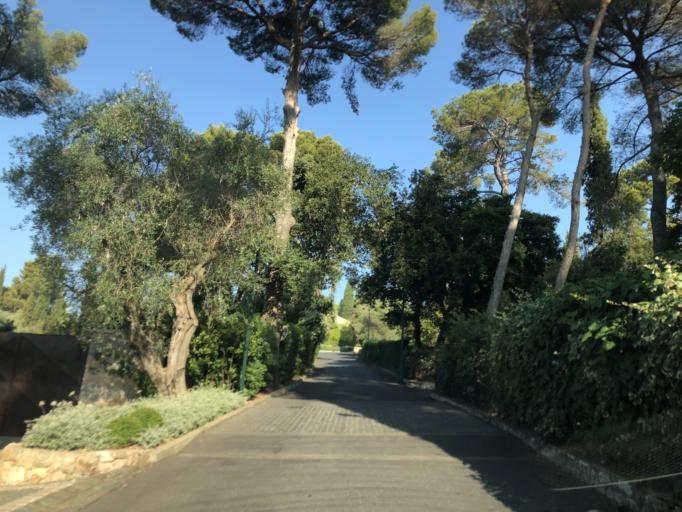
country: FR
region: Provence-Alpes-Cote d'Azur
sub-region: Departement des Alpes-Maritimes
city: Biot
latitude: 43.6235
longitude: 7.0919
